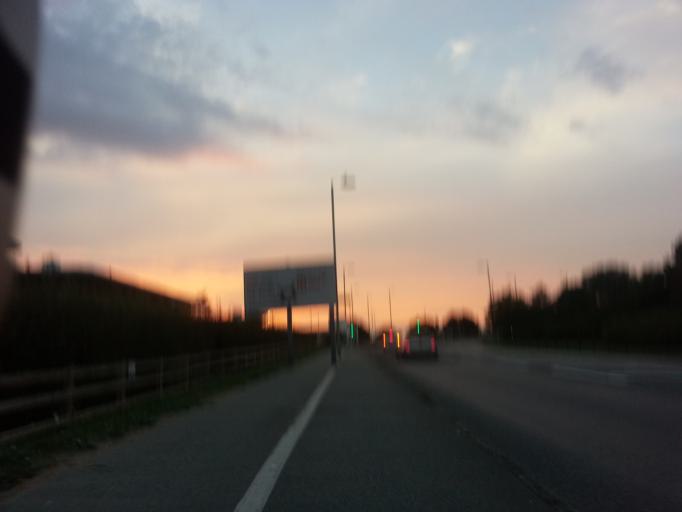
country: GB
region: England
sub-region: Suffolk
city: Kesgrave
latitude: 52.0287
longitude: 1.2030
